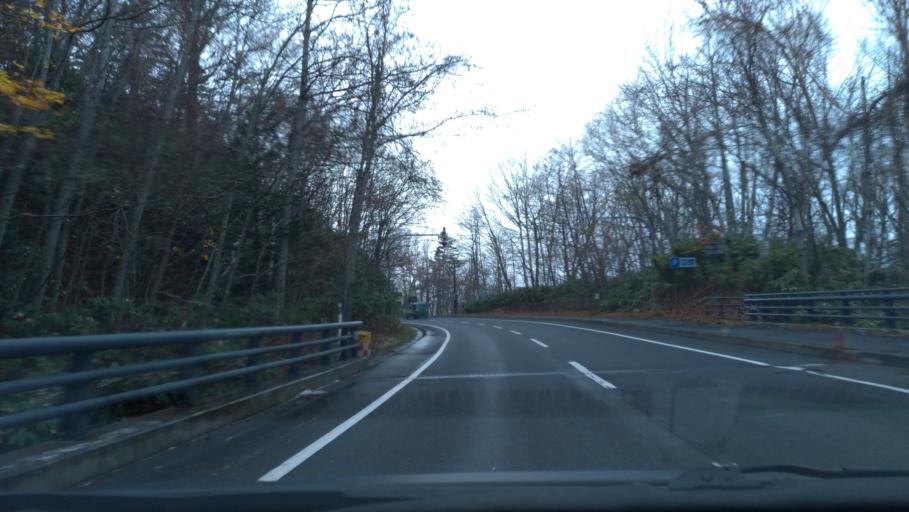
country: JP
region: Hokkaido
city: Shiraoi
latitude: 42.7361
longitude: 141.3529
